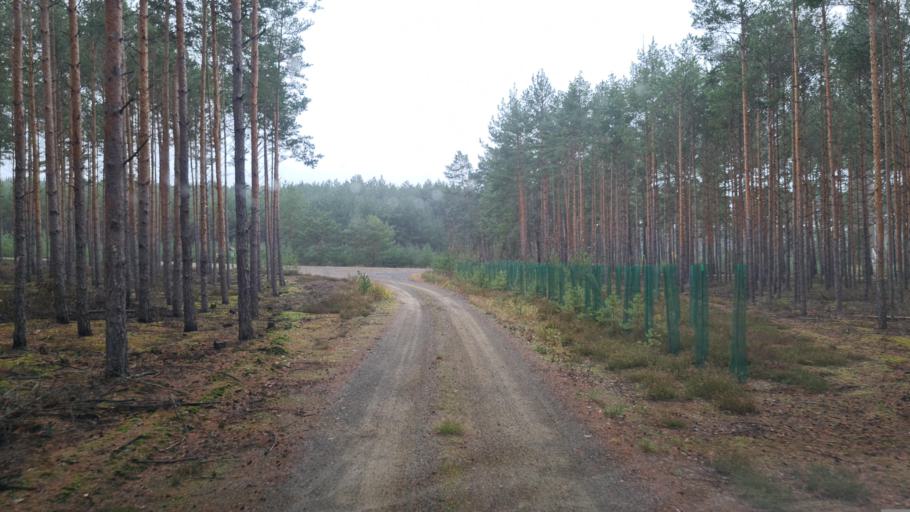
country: DE
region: Brandenburg
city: Sallgast
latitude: 51.6420
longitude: 13.8236
